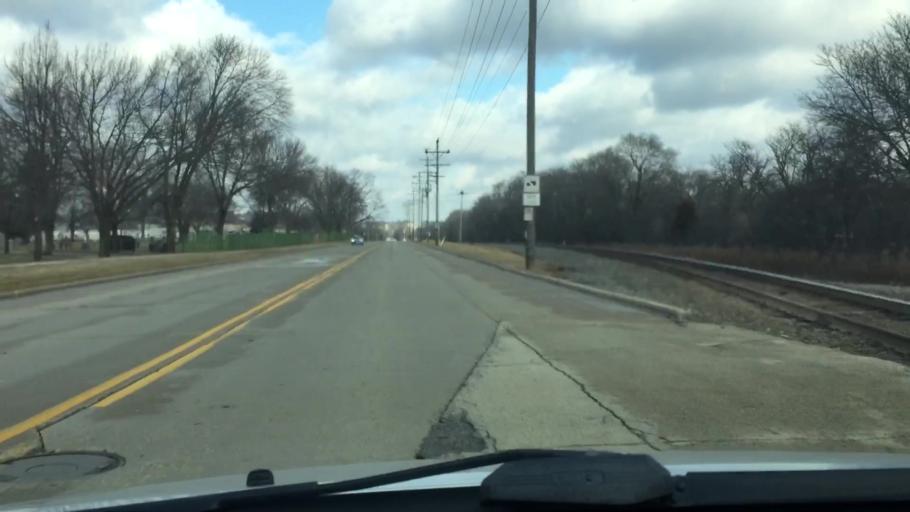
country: US
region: Wisconsin
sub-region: Waukesha County
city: Waukesha
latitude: 42.9941
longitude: -88.2369
